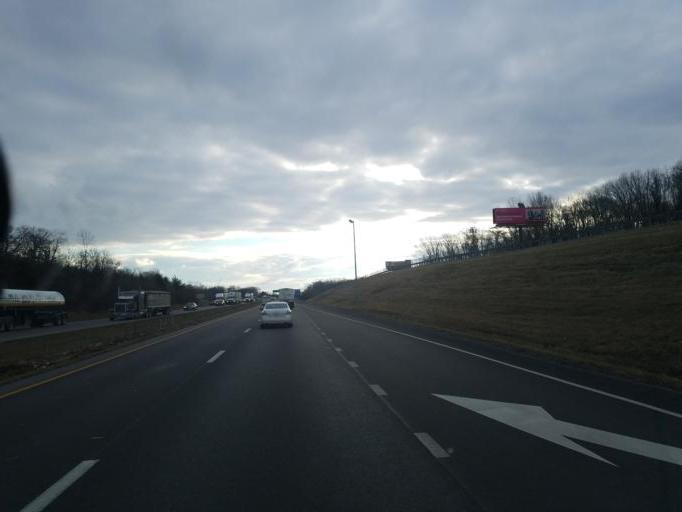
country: US
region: Missouri
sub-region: Saint Louis County
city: Glasgow Village
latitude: 38.7675
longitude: -90.1992
